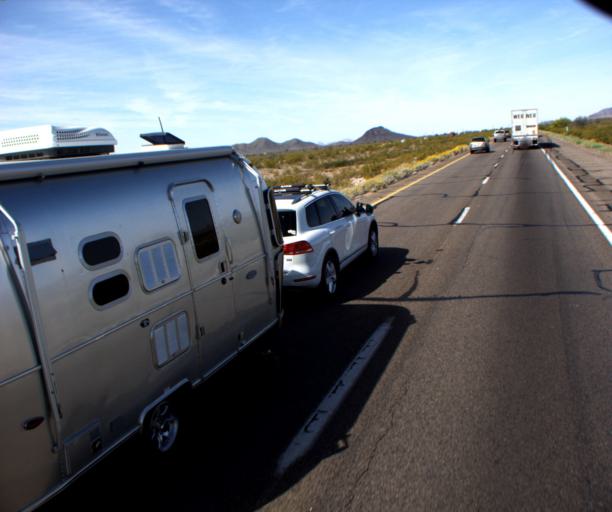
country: US
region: Arizona
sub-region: Maricopa County
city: Buckeye
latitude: 33.5043
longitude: -112.9720
